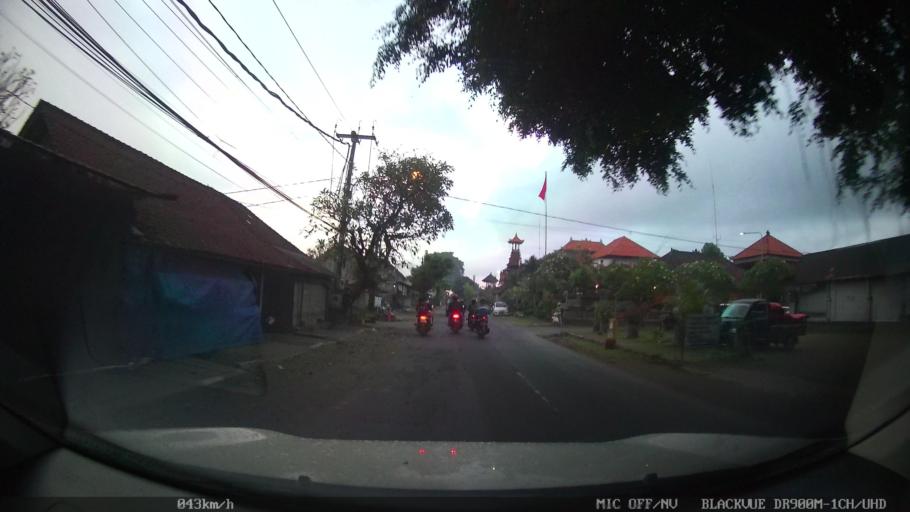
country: ID
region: Bali
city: Banjar Parekan
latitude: -8.5762
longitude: 115.2179
